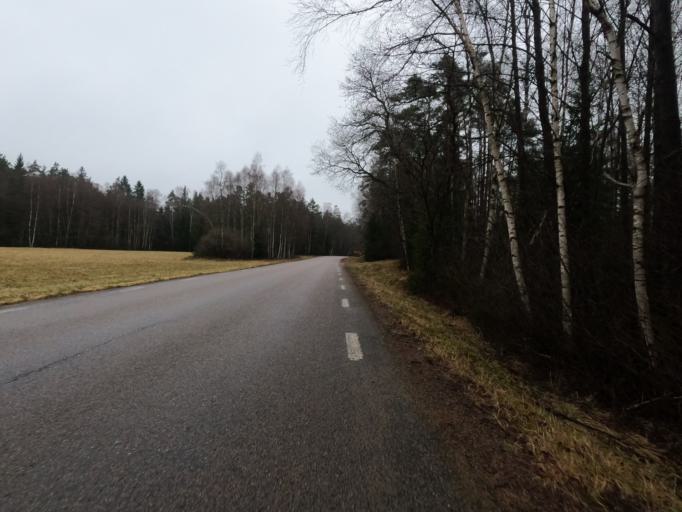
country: SE
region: Halland
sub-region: Hylte Kommun
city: Torup
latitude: 56.7949
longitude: 13.1949
